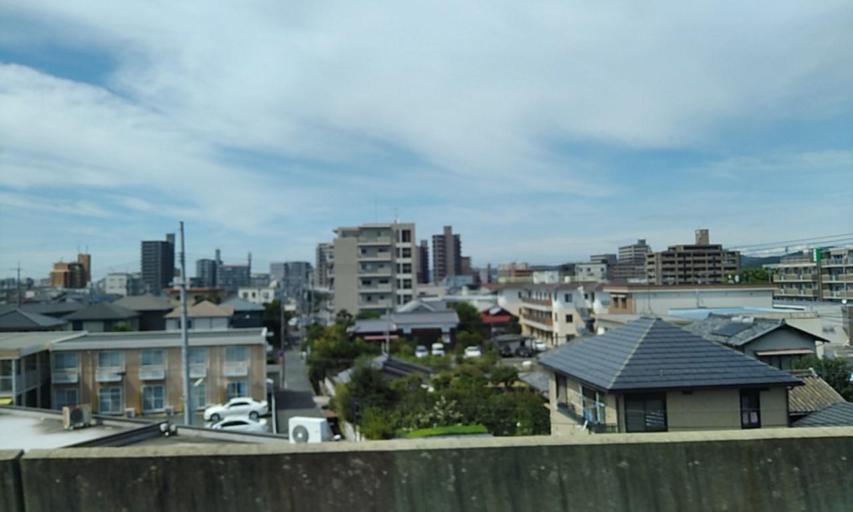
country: JP
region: Okayama
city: Okayama-shi
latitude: 34.6542
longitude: 133.9104
